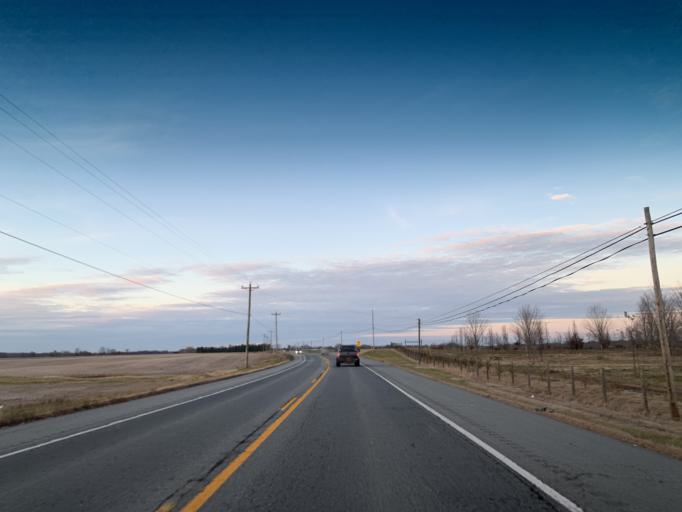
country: US
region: Delaware
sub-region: New Castle County
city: Middletown
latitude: 39.4263
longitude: -75.8603
